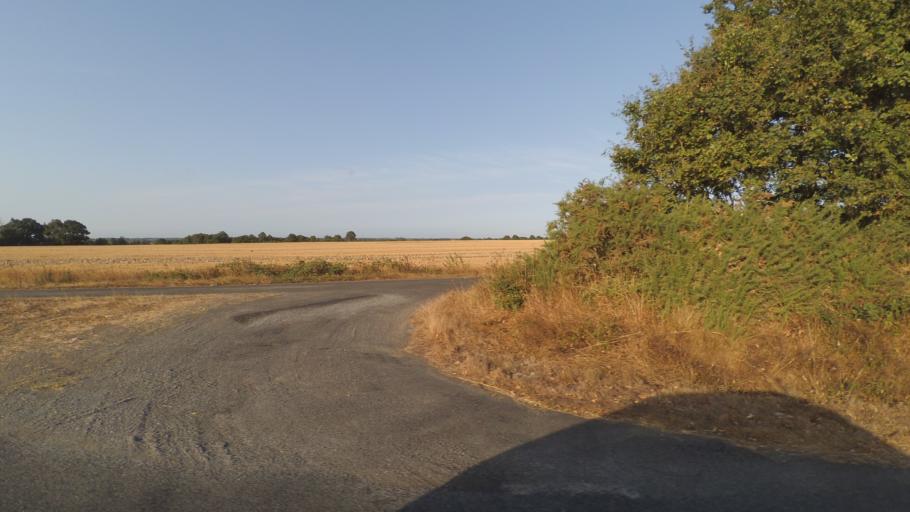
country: FR
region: Pays de la Loire
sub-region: Departement de la Loire-Atlantique
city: Vieillevigne
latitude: 46.9935
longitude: -1.4605
